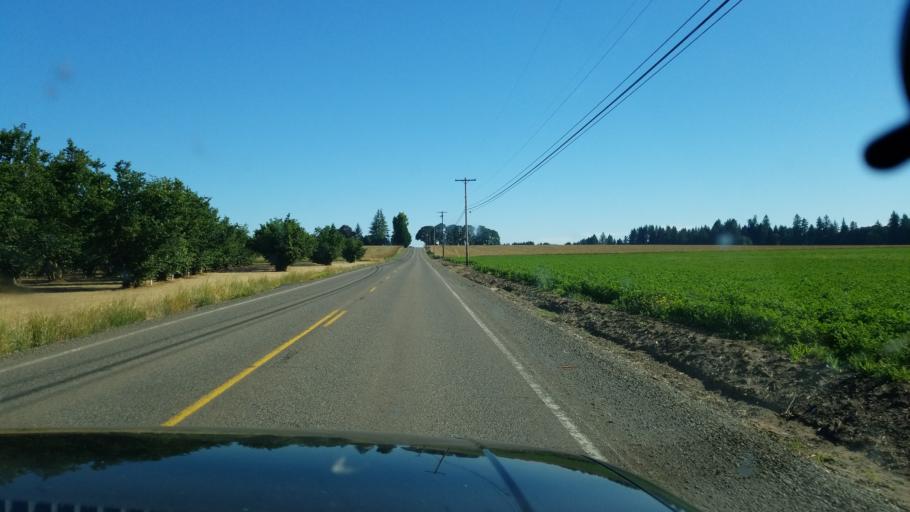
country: US
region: Oregon
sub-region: Yamhill County
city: Carlton
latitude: 45.2632
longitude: -123.2047
